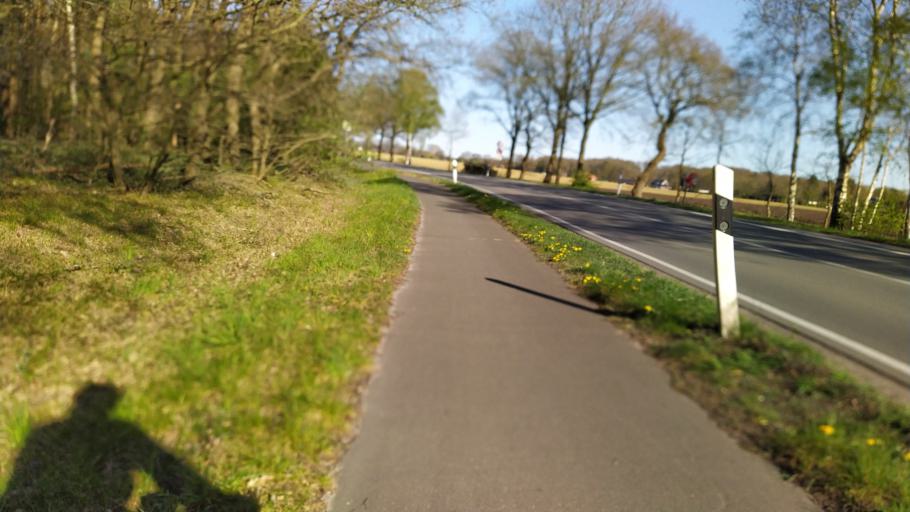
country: DE
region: Lower Saxony
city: Hamersen
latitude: 53.2800
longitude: 9.4798
